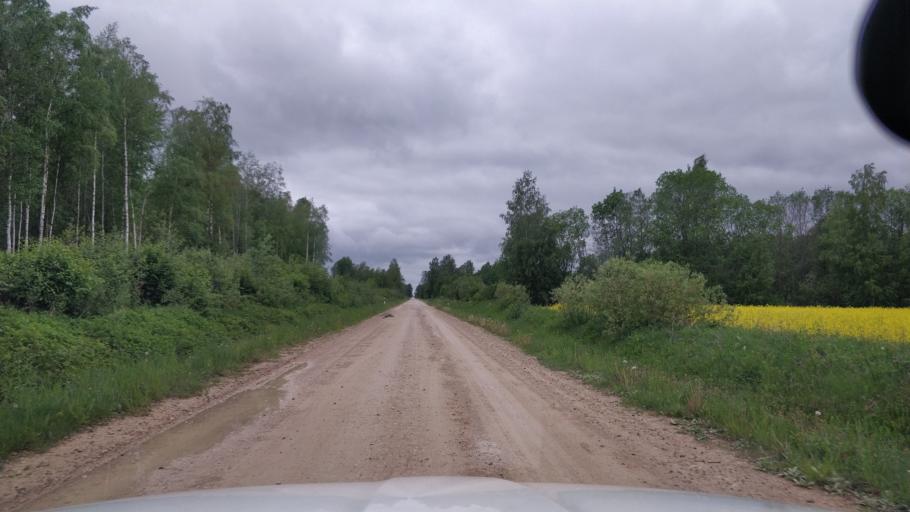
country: EE
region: Raplamaa
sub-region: Maerjamaa vald
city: Marjamaa
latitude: 58.7172
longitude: 24.2887
